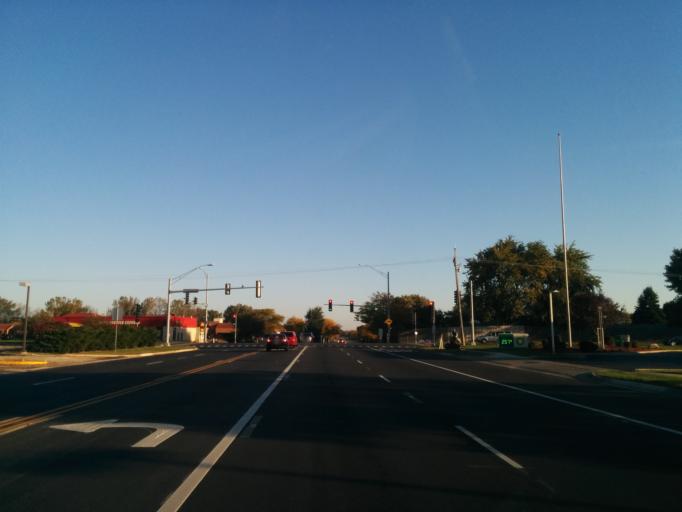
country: US
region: Illinois
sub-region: DuPage County
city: Carol Stream
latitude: 41.9398
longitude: -88.1504
